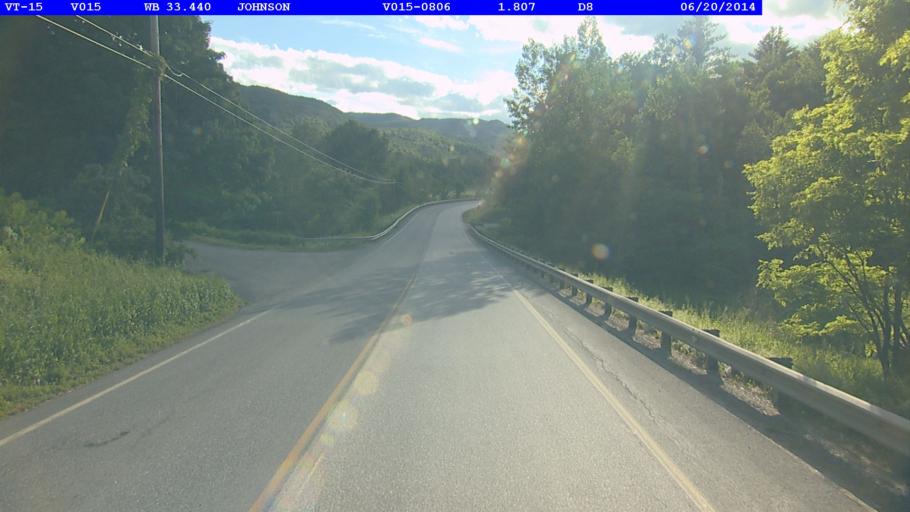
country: US
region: Vermont
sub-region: Lamoille County
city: Johnson
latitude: 44.6423
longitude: -72.7209
